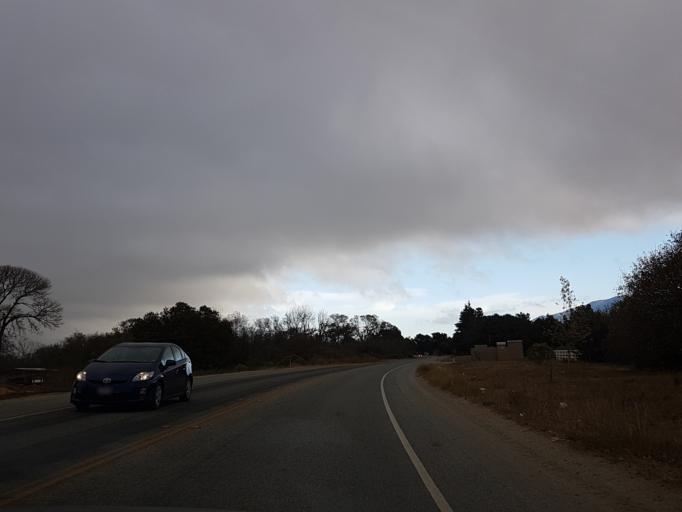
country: US
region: California
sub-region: Monterey County
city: Salinas
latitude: 36.6057
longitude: -121.6403
